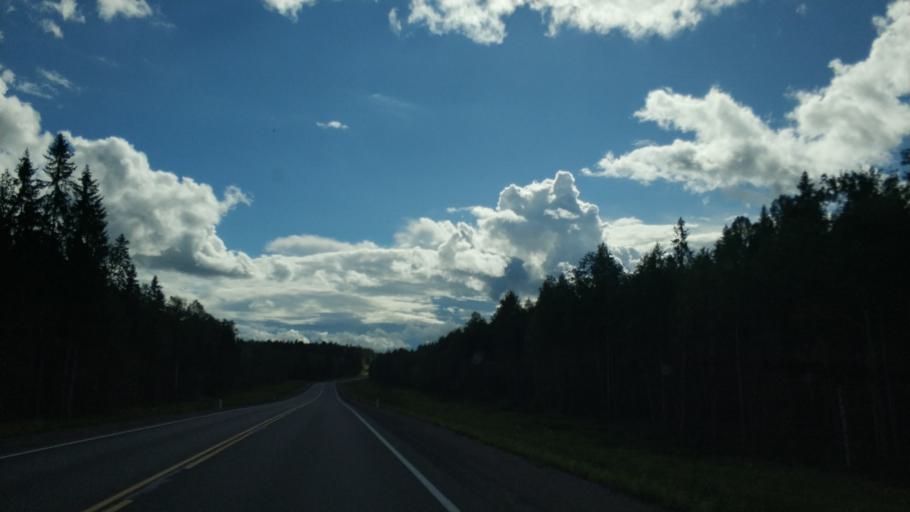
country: RU
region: Republic of Karelia
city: Ruskeala
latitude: 61.8604
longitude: 30.6521
